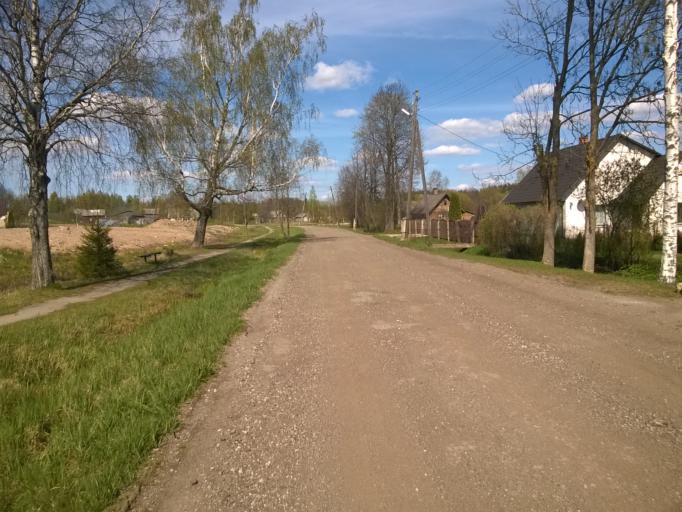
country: LV
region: Vilanu
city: Vilani
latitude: 56.5541
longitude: 26.9325
